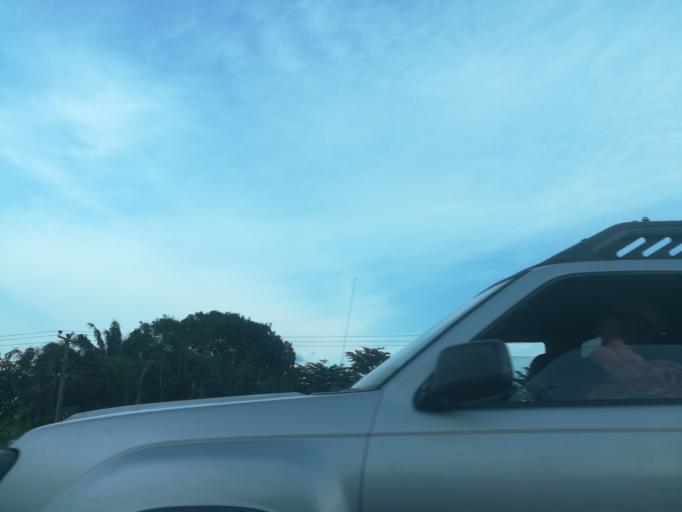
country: NG
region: Lagos
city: Ebute Ikorodu
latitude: 6.6204
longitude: 3.4798
